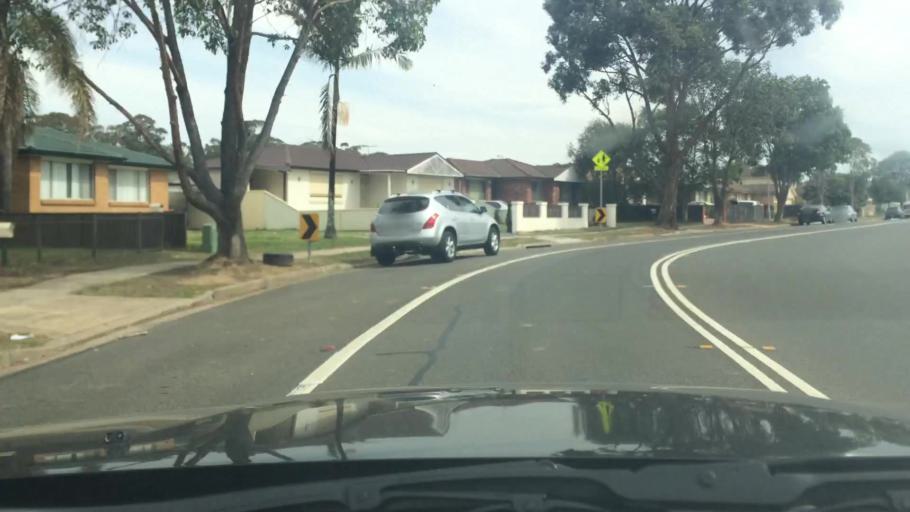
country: AU
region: New South Wales
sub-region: Fairfield
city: Cabramatta West
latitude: -33.8670
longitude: 150.8949
